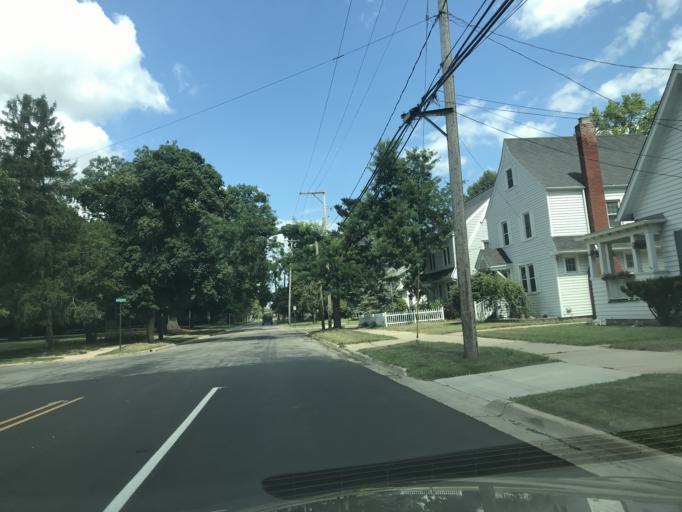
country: US
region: Michigan
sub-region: Jackson County
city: Jackson
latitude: 42.2251
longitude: -84.4183
